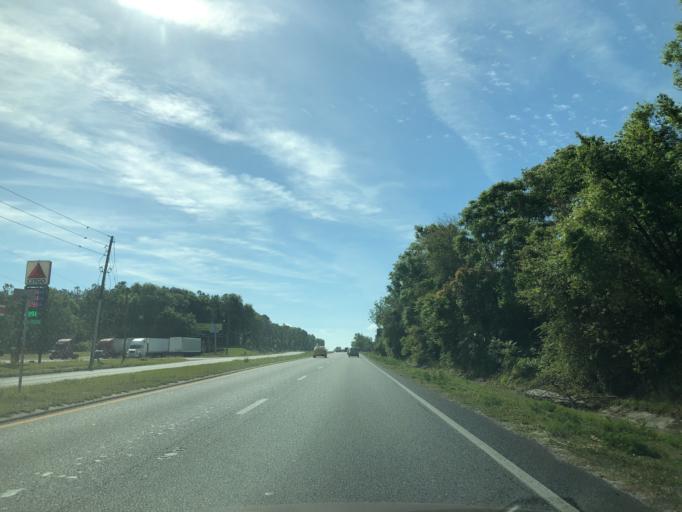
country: US
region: Florida
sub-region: Orange County
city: Zellwood
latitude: 28.7228
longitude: -81.5968
